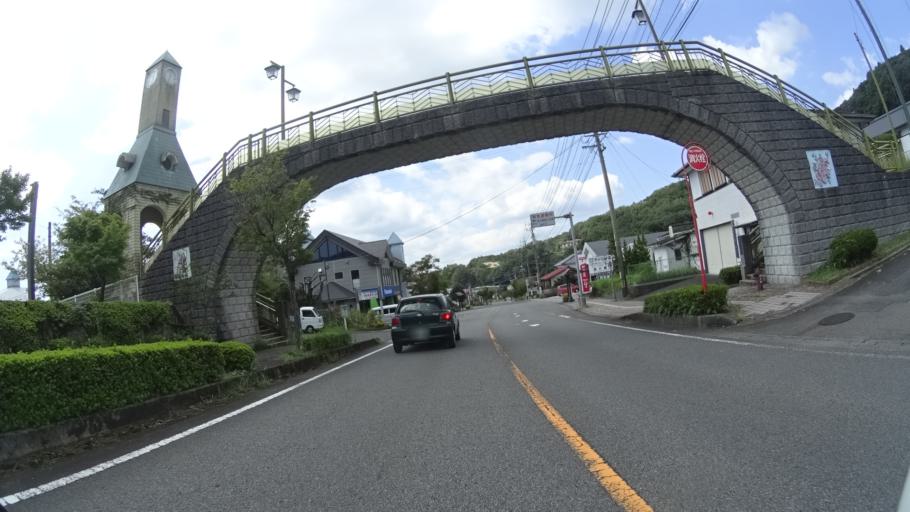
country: JP
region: Kagoshima
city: Kokubu-matsuki
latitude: 31.8861
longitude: 130.8200
